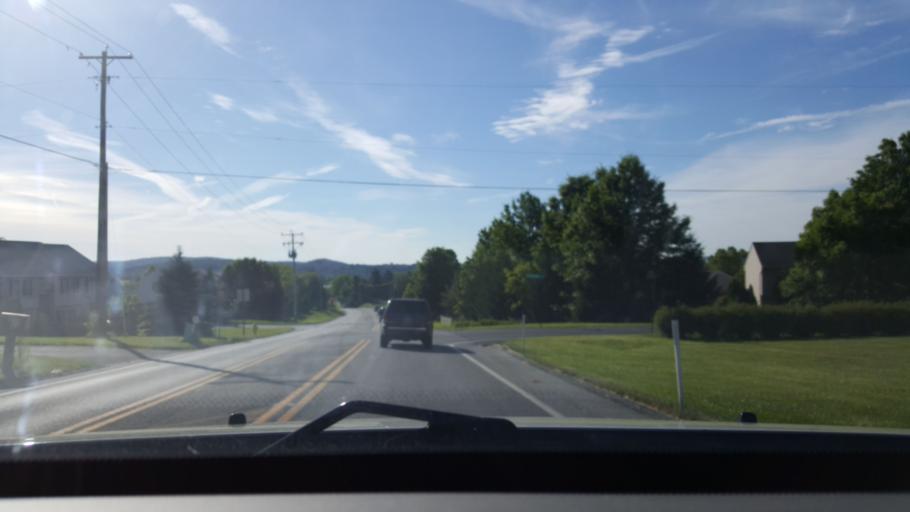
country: US
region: Pennsylvania
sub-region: York County
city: Emigsville
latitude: 40.0037
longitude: -76.7590
